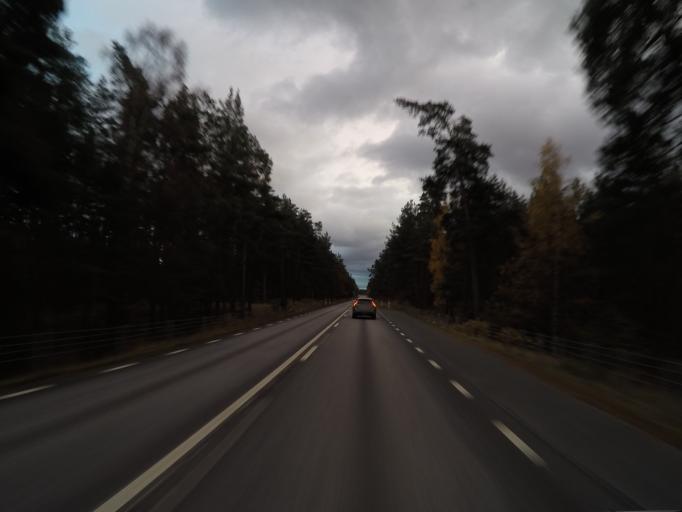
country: SE
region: Skane
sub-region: Kristianstads Kommun
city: Degeberga
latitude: 55.8562
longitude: 14.0926
